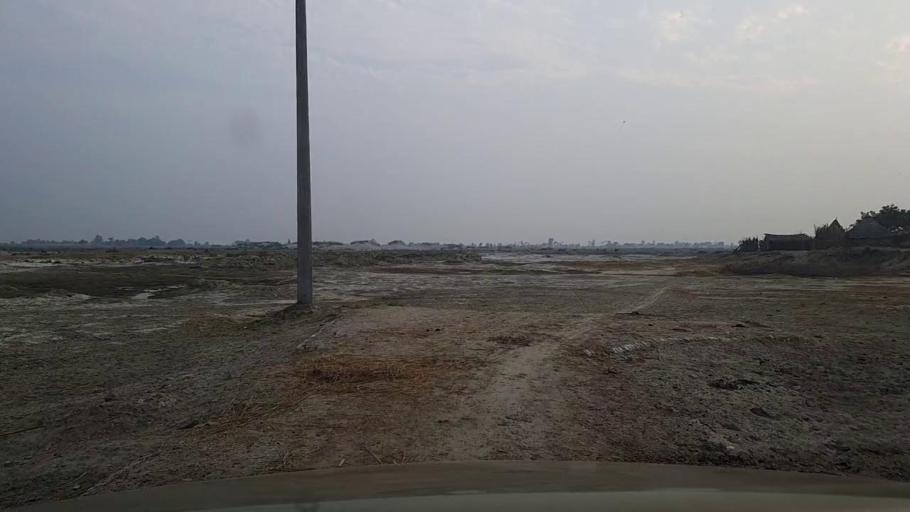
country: PK
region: Sindh
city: Sanghar
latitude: 26.2299
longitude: 68.9427
